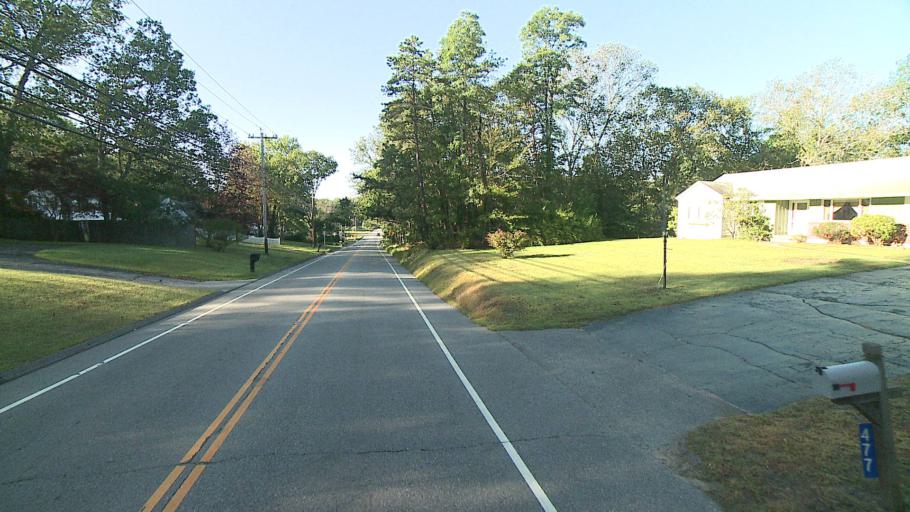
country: US
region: Connecticut
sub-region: Windham County
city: East Brooklyn
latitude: 41.7711
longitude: -71.8977
